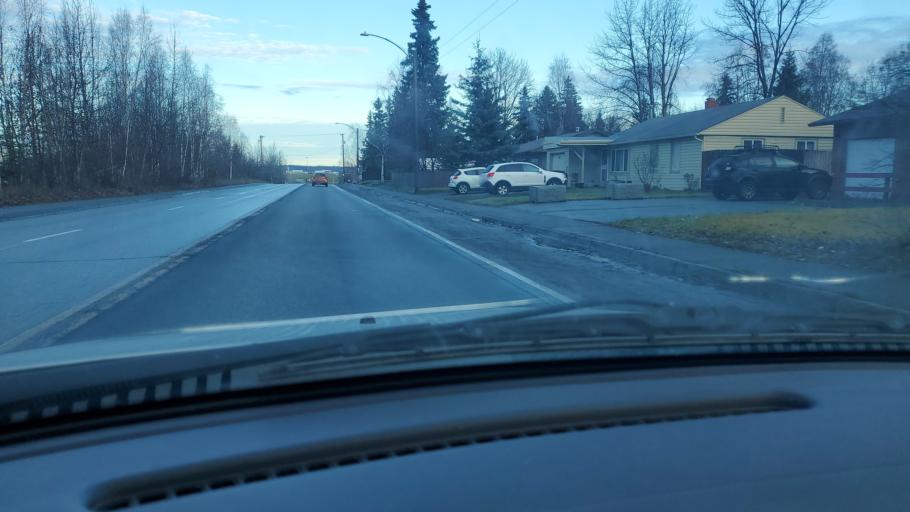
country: US
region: Alaska
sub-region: Anchorage Municipality
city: Anchorage
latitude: 61.2042
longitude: -149.8383
